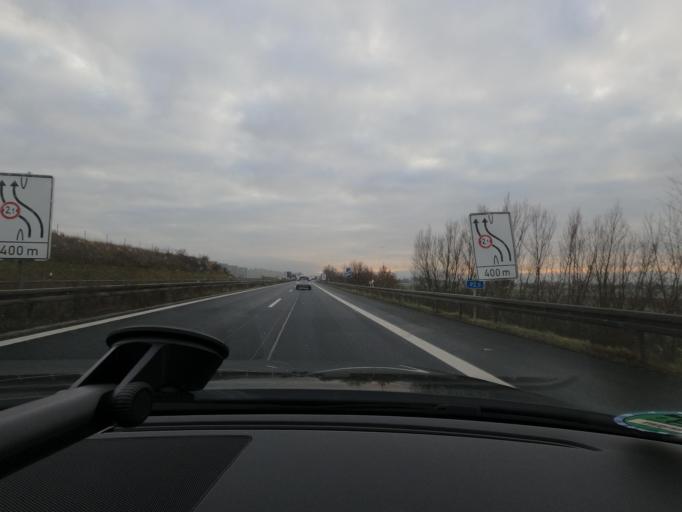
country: DE
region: Bavaria
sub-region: Upper Franconia
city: Kemmern
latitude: 49.9644
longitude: 10.8798
